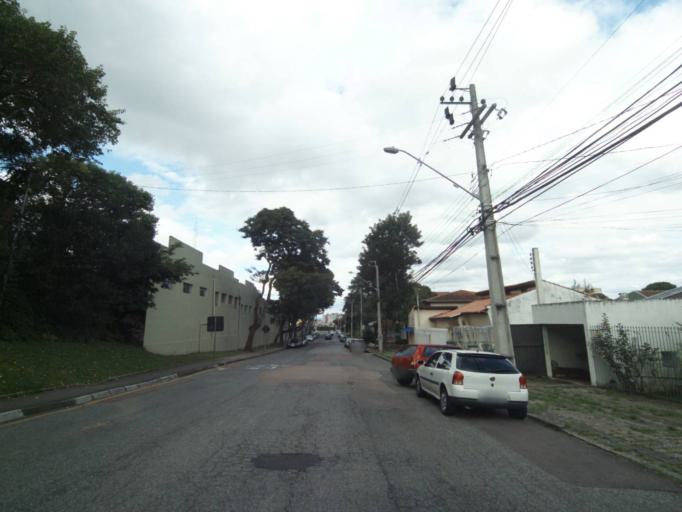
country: BR
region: Parana
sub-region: Curitiba
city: Curitiba
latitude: -25.4197
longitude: -49.2794
